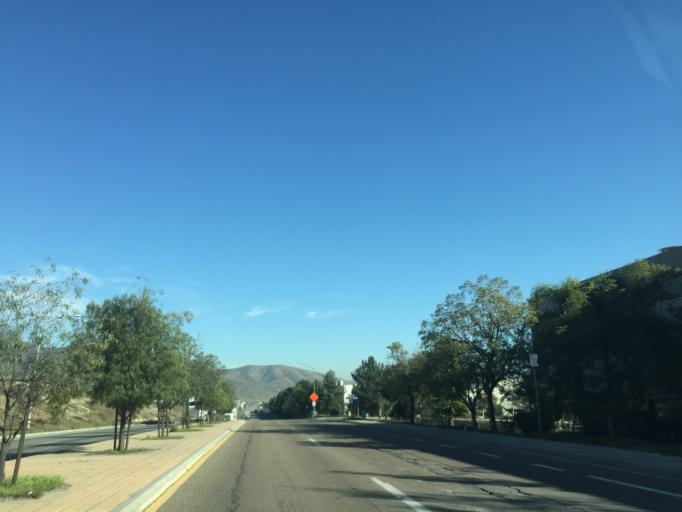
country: MX
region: Baja California
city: Tijuana
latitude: 32.5601
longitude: -116.9331
